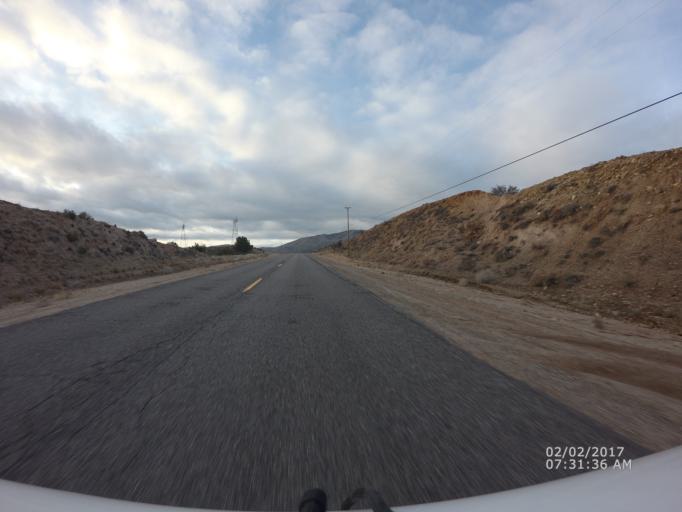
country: US
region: California
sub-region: Los Angeles County
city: Littlerock
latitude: 34.5088
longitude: -118.0452
